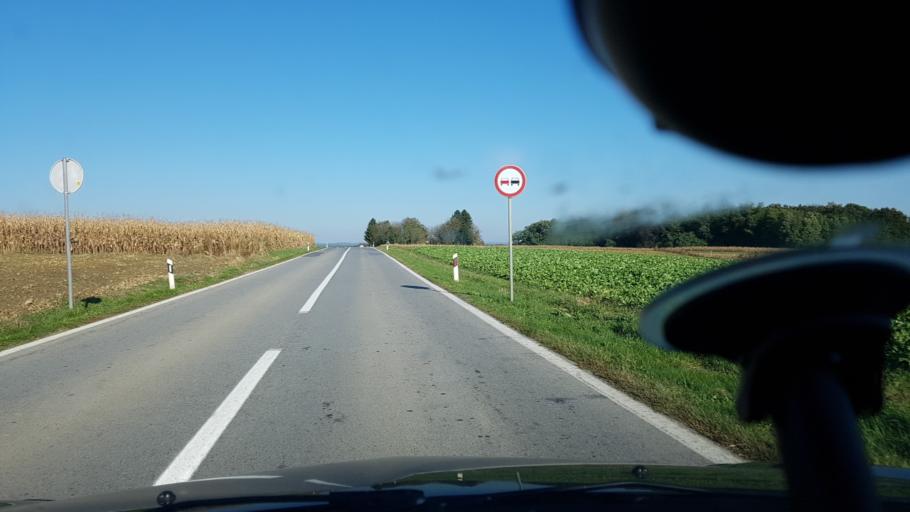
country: HR
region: Bjelovarsko-Bilogorska
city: Gudovac
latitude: 45.8194
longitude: 16.7288
